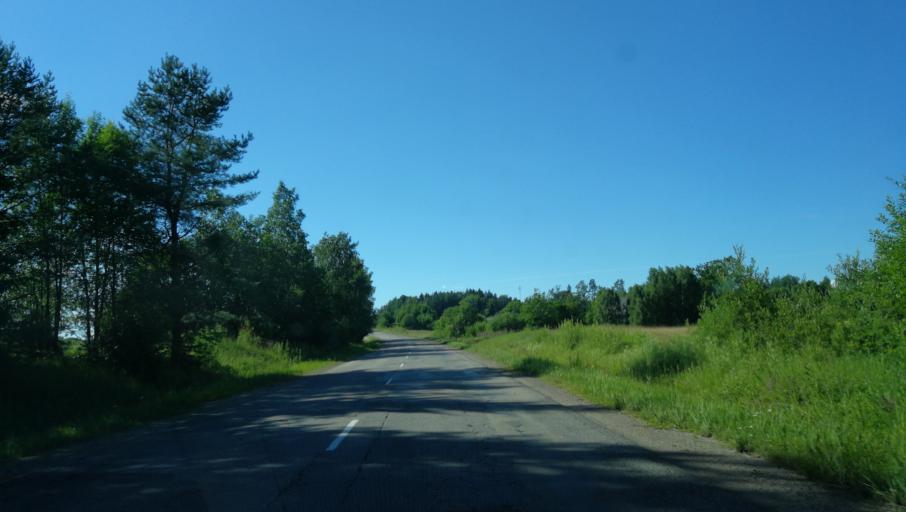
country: LV
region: Jaunpiebalga
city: Jaunpiebalga
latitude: 56.9785
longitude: 26.0375
